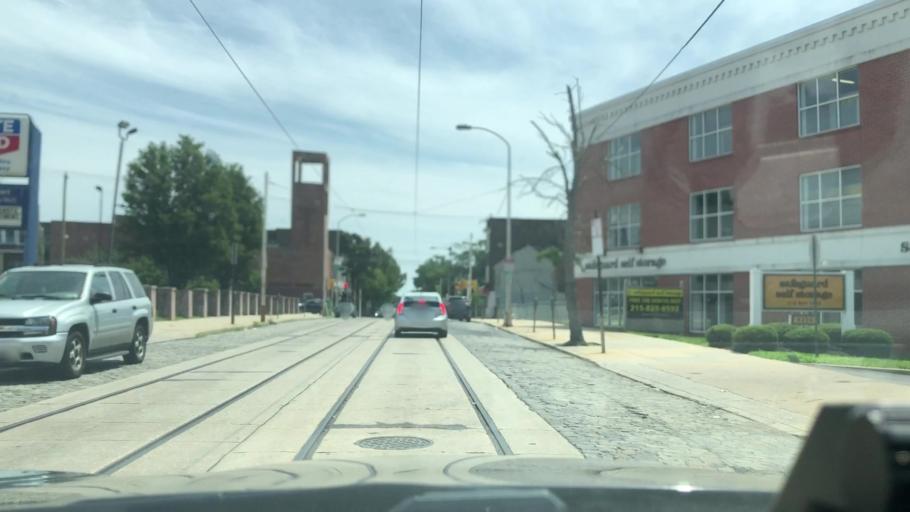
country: US
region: Pennsylvania
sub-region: Montgomery County
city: Wyndmoor
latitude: 40.0428
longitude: -75.1806
